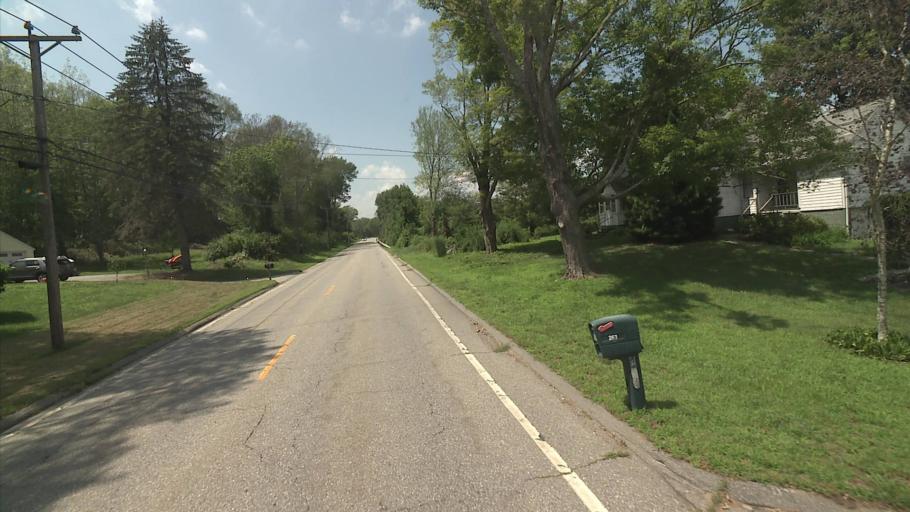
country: US
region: Connecticut
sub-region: New London County
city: Preston City
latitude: 41.5314
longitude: -71.9979
